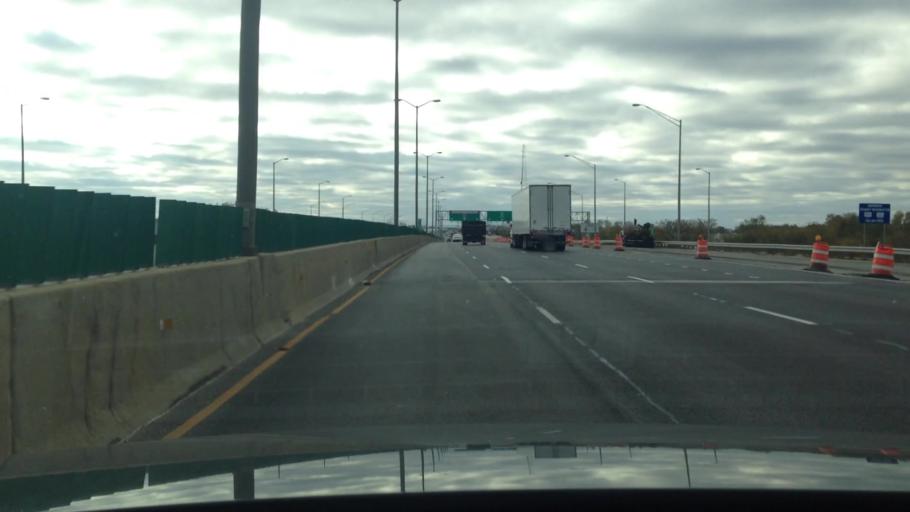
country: US
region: Illinois
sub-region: DuPage County
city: Glendale Heights
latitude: 41.9319
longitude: -88.0377
